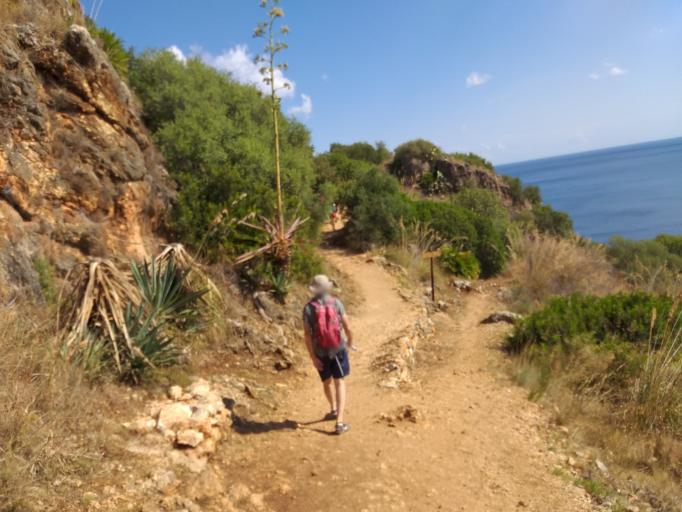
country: IT
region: Sicily
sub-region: Trapani
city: Castelluzzo
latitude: 38.0840
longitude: 12.8074
